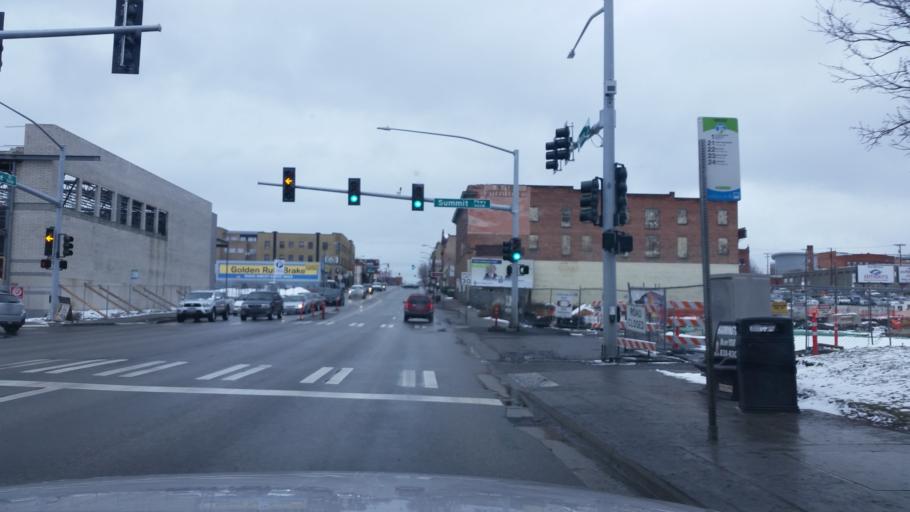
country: US
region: Washington
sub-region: Spokane County
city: Spokane
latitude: 47.6621
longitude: -117.4265
